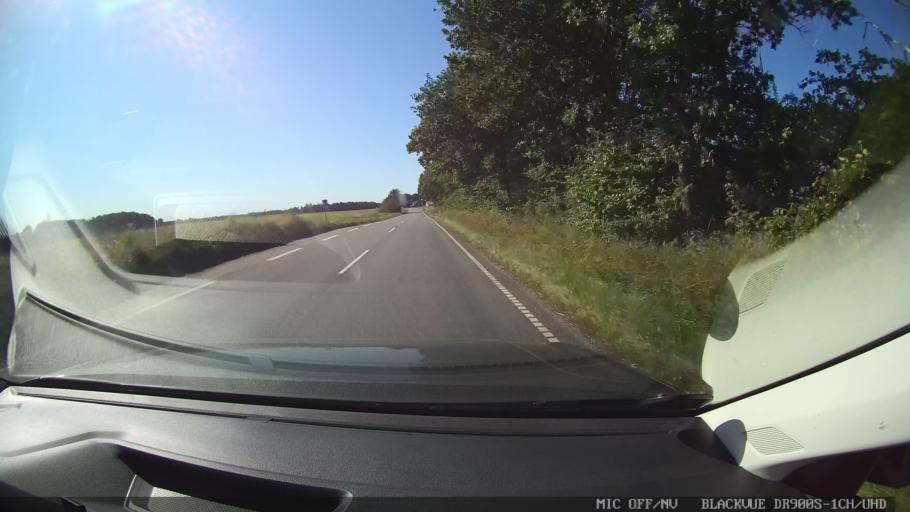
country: DK
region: North Denmark
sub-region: Mariagerfjord Kommune
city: Mariager
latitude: 56.6348
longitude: 9.9190
